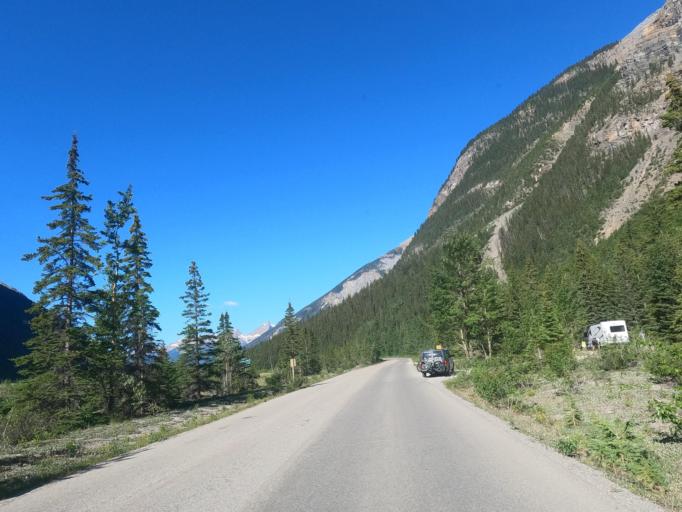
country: CA
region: Alberta
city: Lake Louise
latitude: 51.4199
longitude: -116.4449
